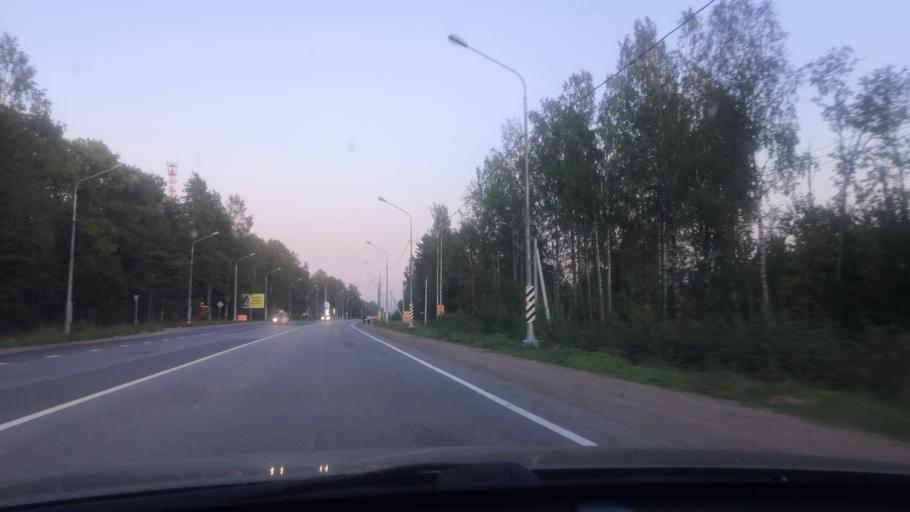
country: RU
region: St.-Petersburg
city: Beloostrov
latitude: 60.1933
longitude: 30.0792
